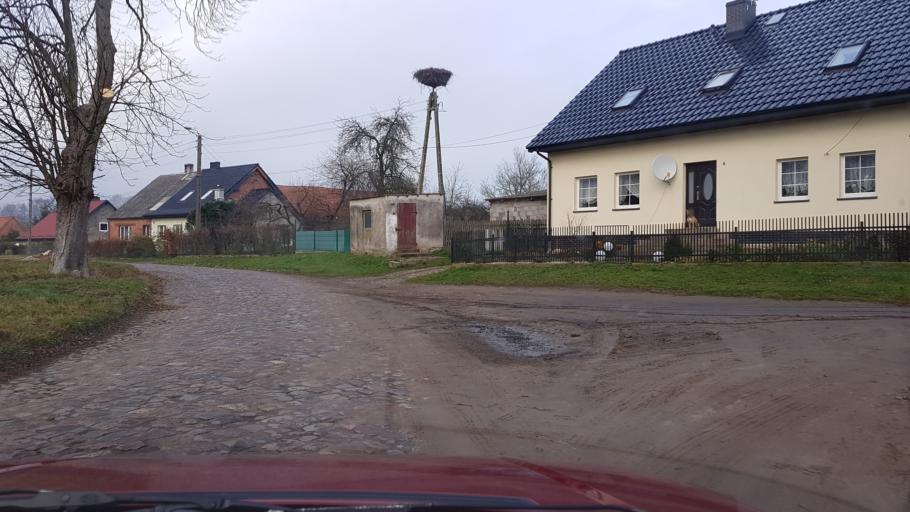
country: PL
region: West Pomeranian Voivodeship
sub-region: Powiat bialogardzki
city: Tychowo
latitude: 53.9786
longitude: 16.3152
